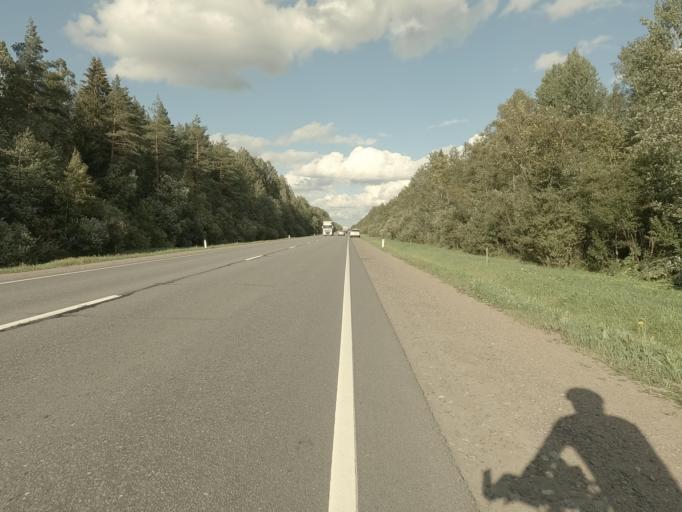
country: RU
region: Leningrad
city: Nikol'skoye
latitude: 59.6486
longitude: 30.8471
